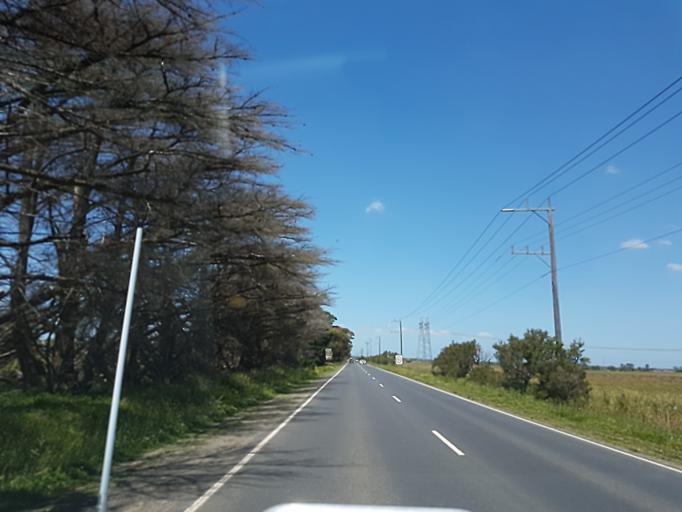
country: AU
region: Victoria
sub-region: Cardinia
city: Pakenham South
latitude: -38.1047
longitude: 145.4875
